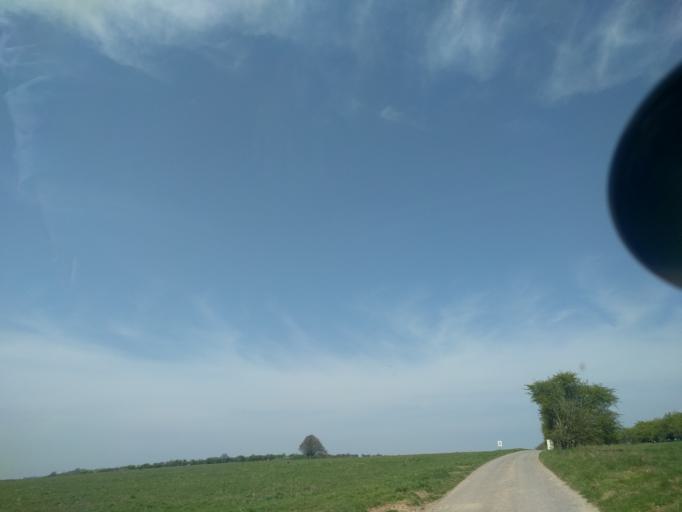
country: GB
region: England
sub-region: Wiltshire
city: Edington
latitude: 51.2465
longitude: -2.1005
